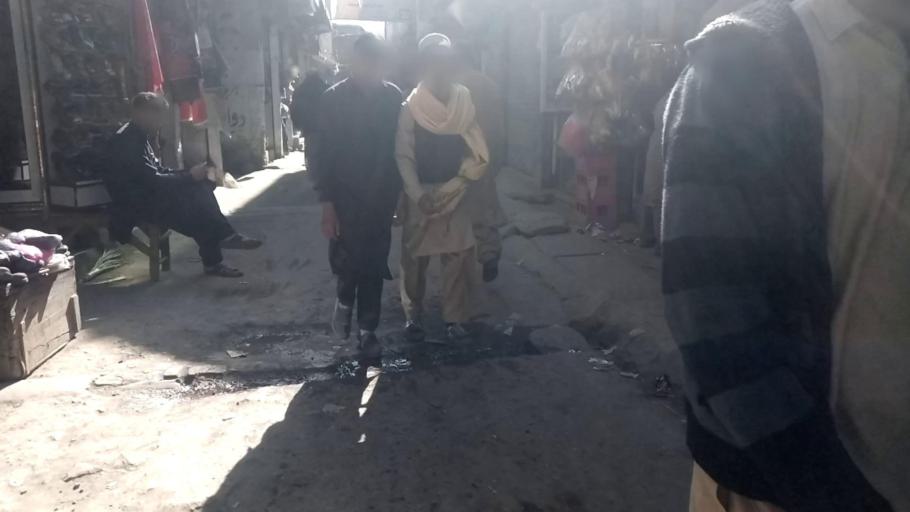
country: PK
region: Khyber Pakhtunkhwa
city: Mingora
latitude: 34.7821
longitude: 72.3603
